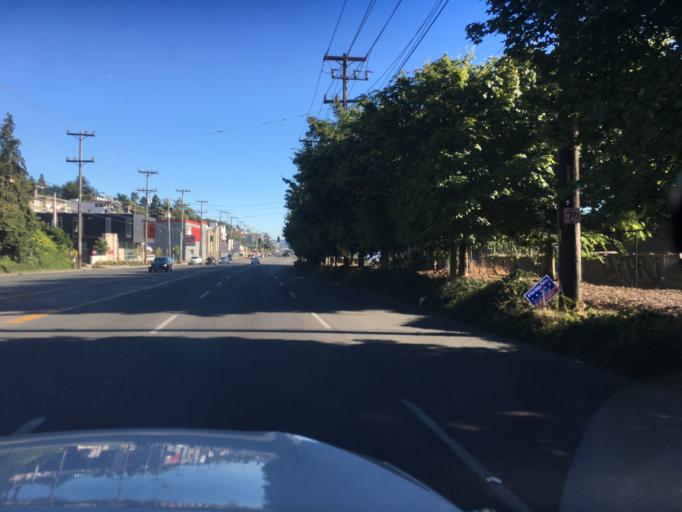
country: US
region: Washington
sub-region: King County
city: Seattle
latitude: 47.6462
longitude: -122.3764
